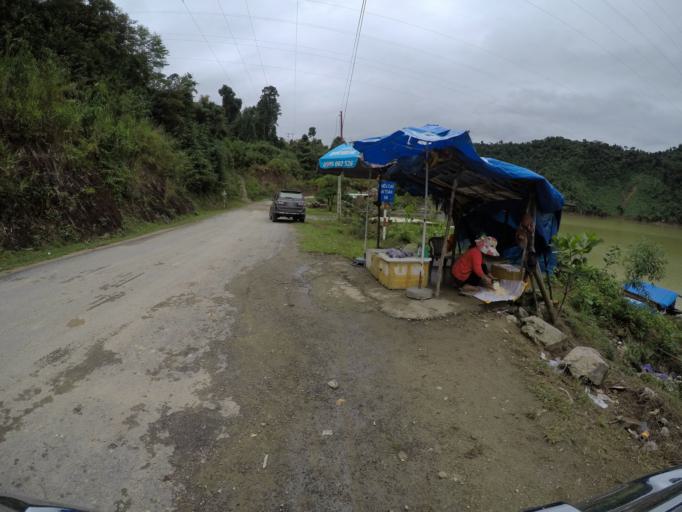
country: VN
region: Quang Nam
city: Thanh My
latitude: 15.6588
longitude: 107.6212
